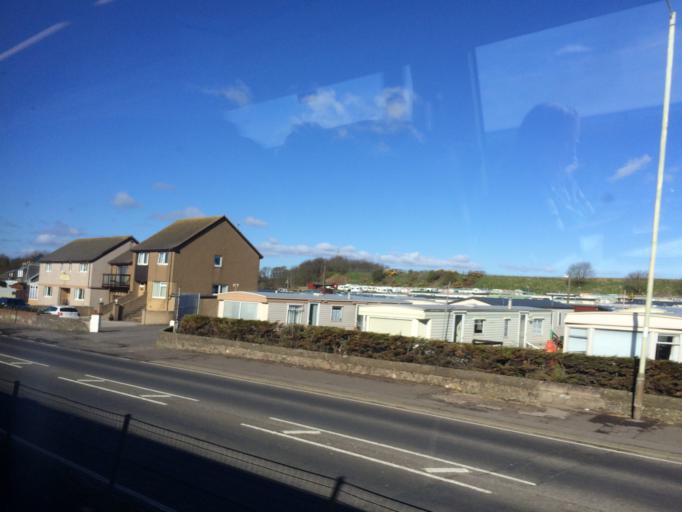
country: GB
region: Scotland
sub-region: Angus
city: Arbroath
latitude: 56.5469
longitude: -2.6163
